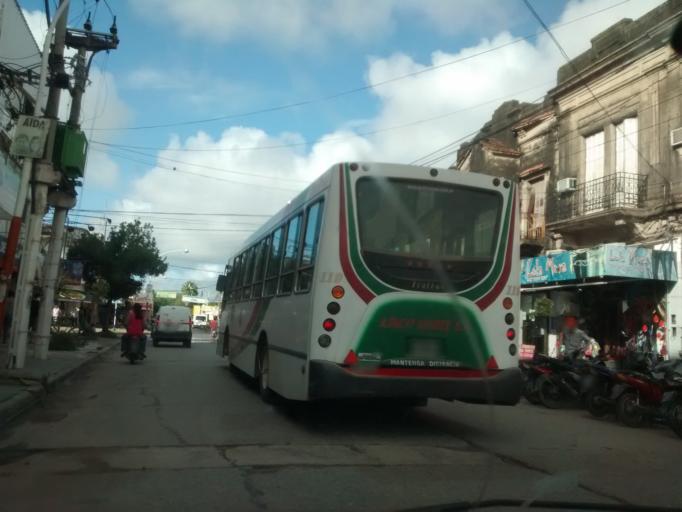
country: AR
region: Chaco
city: Resistencia
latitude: -27.4524
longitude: -58.9897
